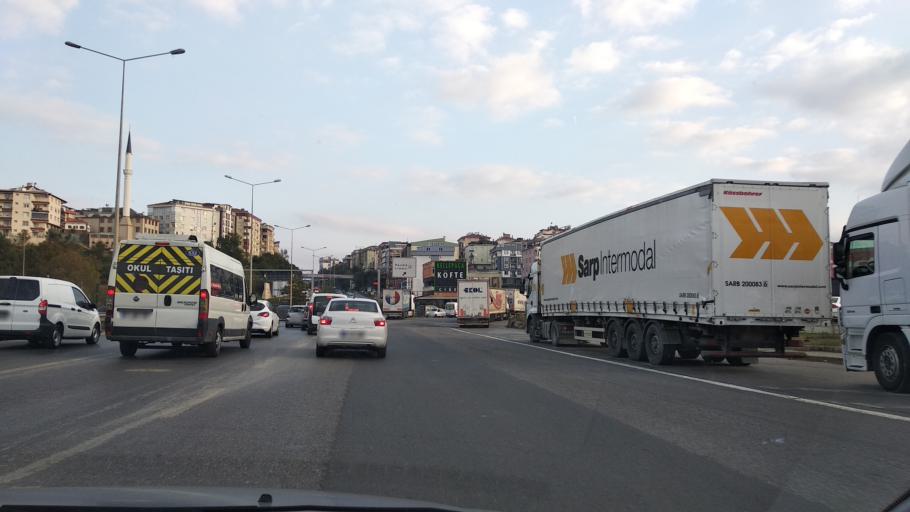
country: TR
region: Istanbul
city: Pendik
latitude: 40.8640
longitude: 29.2754
